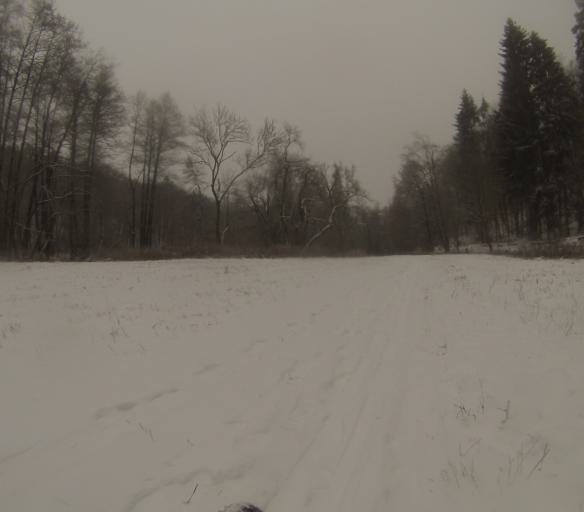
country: CZ
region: South Moravian
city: Strelice
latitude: 49.1349
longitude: 16.4967
